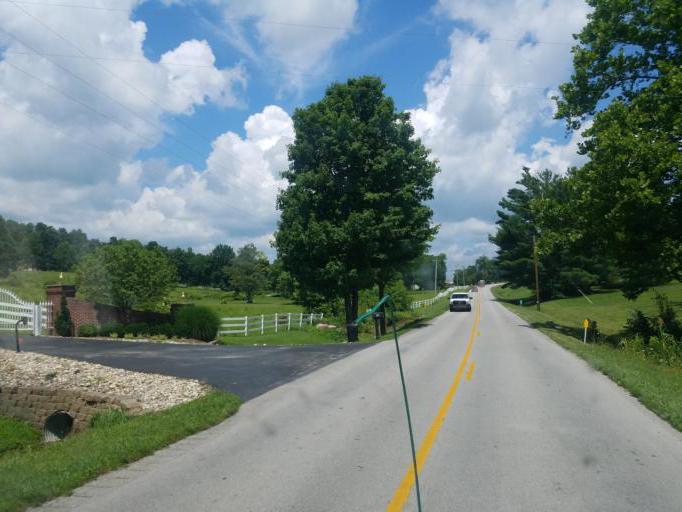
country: US
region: Kentucky
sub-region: Grayson County
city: Leitchfield
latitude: 37.4989
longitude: -86.3081
